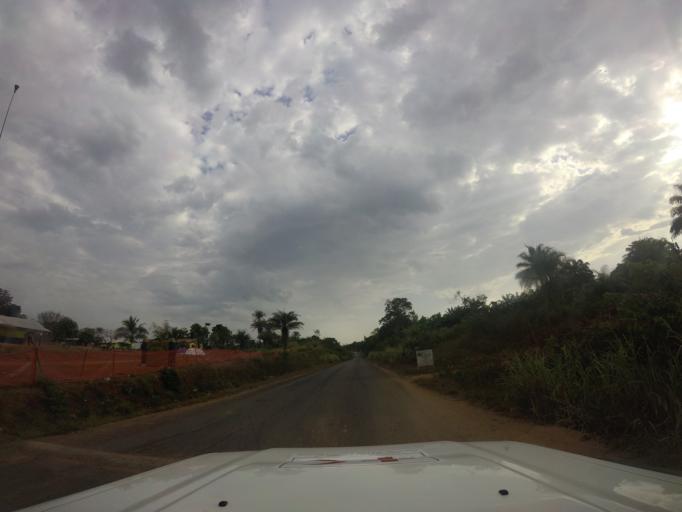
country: LR
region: Grand Cape Mount
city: Robertsport
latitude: 6.7689
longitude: -11.1483
